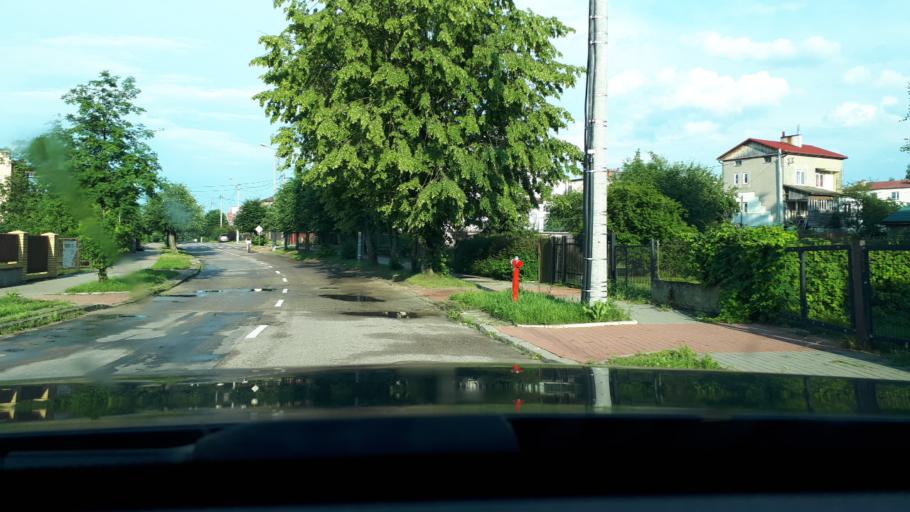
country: PL
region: Podlasie
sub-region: Powiat bialostocki
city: Suprasl
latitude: 53.2061
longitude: 23.3292
